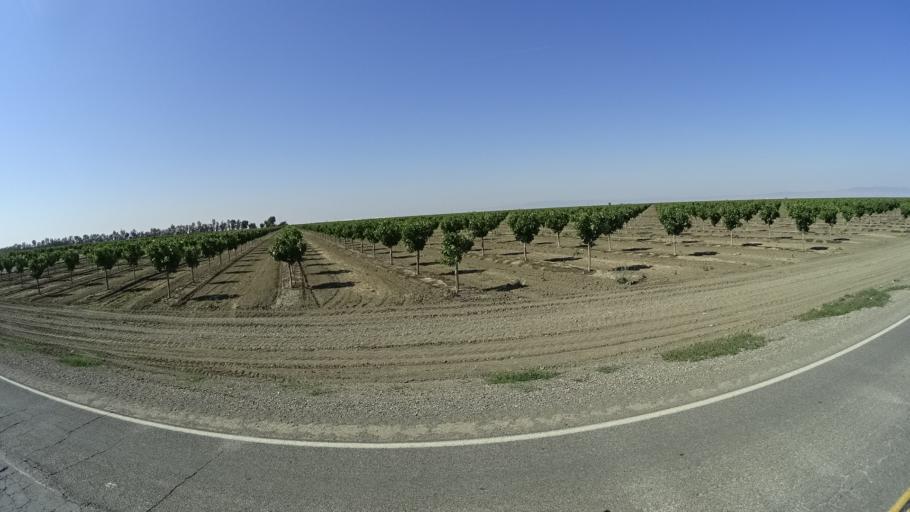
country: US
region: California
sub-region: Fresno County
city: Riverdale
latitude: 36.3861
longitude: -119.9417
